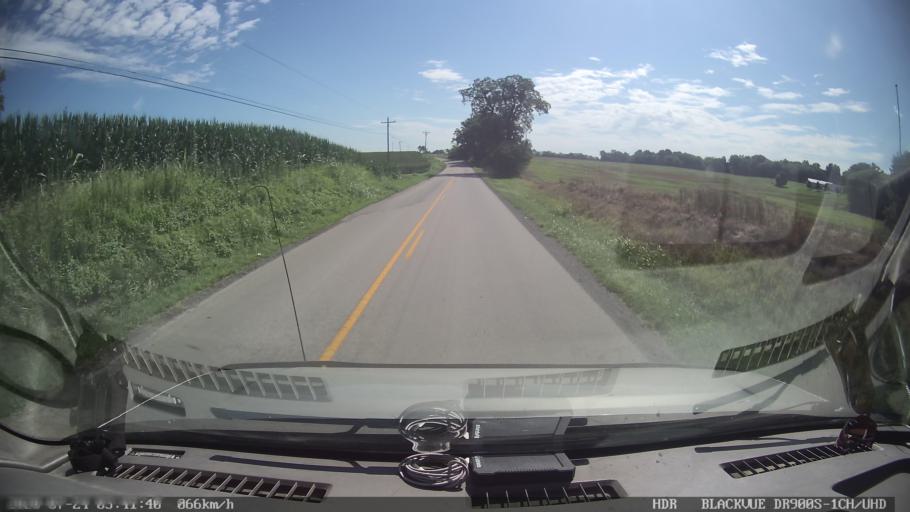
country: US
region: Kentucky
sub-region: Todd County
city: Guthrie
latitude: 36.7347
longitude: -87.2553
